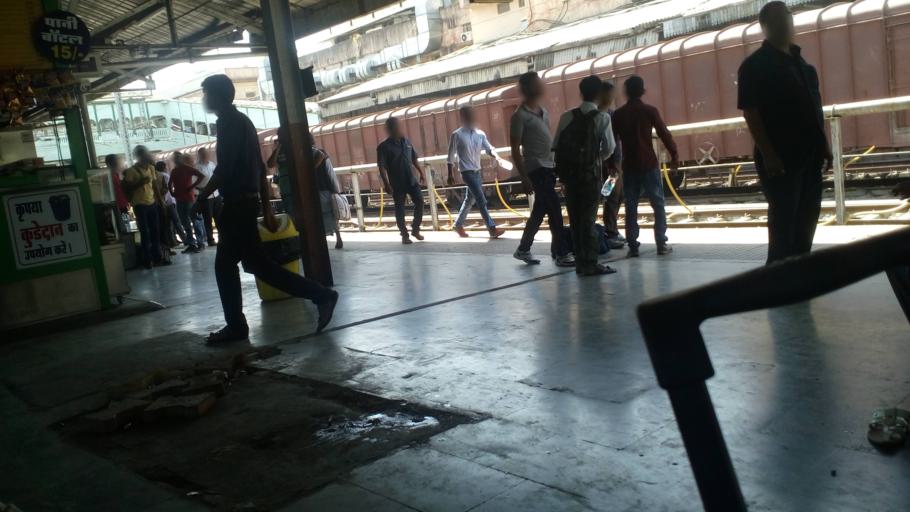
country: IN
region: Maharashtra
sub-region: Nagpur Division
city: Nagpur
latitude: 21.1520
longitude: 79.0885
